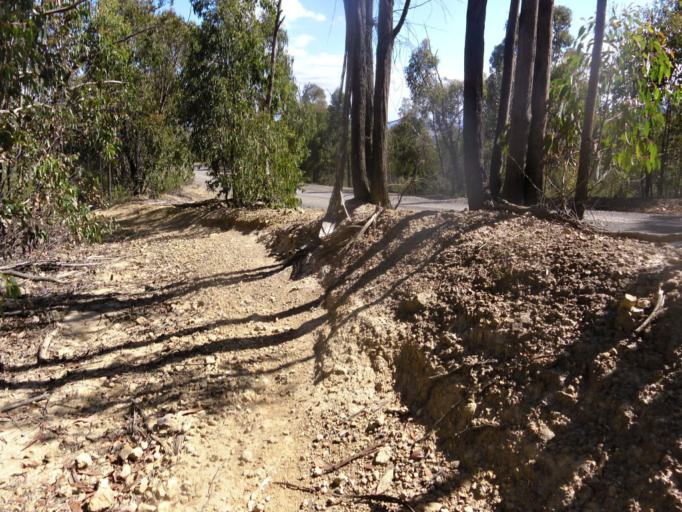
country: AU
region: Victoria
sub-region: Nillumbik
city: Saint Andrews
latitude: -37.5263
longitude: 145.3002
